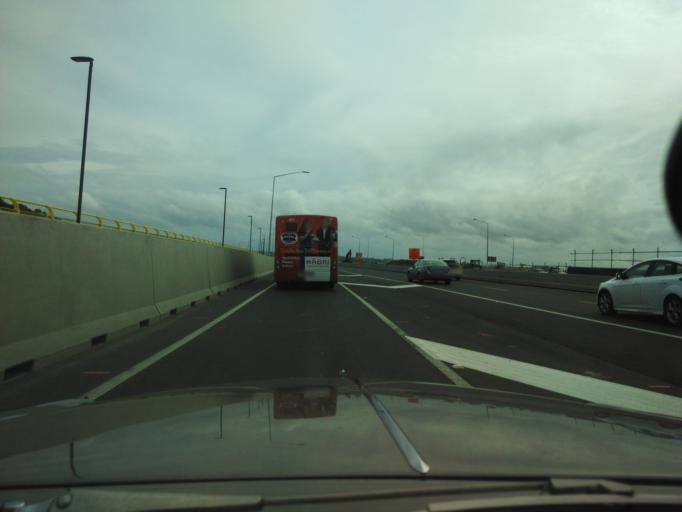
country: NZ
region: Auckland
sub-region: Auckland
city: Rosebank
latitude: -36.8723
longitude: 174.6996
